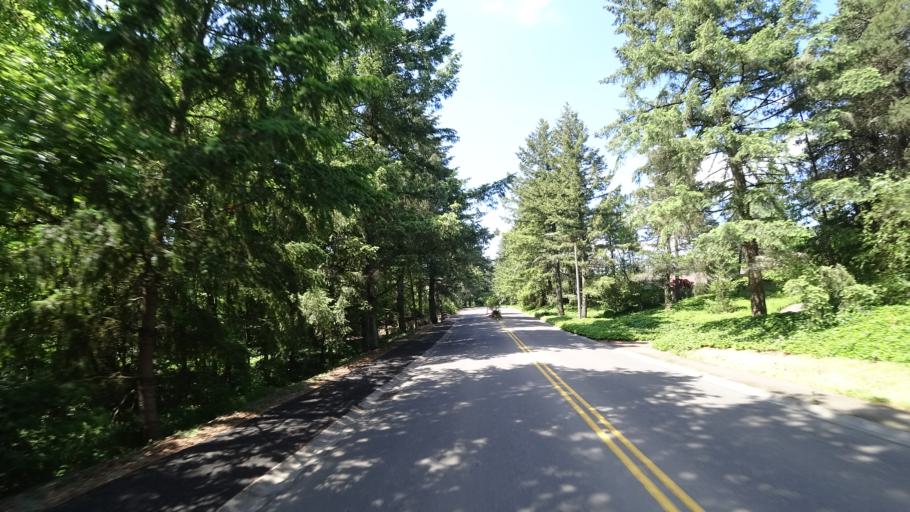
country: US
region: Oregon
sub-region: Clackamas County
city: Lake Oswego
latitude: 45.4314
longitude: -122.7071
